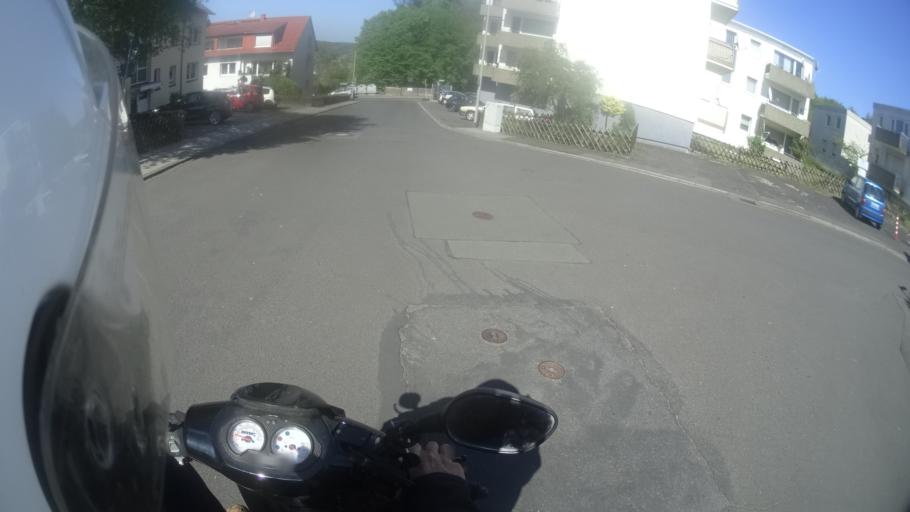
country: DE
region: Hesse
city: Taunusstein
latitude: 50.1318
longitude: 8.1466
